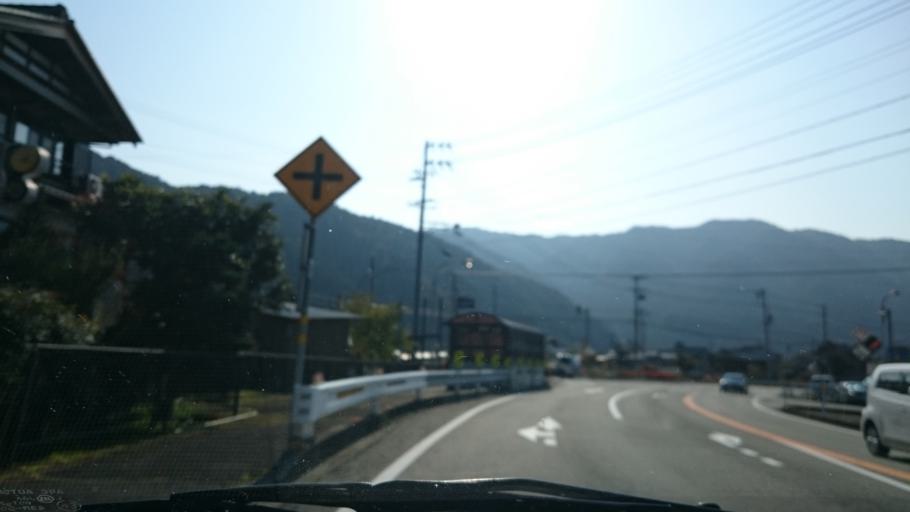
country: JP
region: Gifu
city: Nakatsugawa
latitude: 35.7627
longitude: 137.3197
